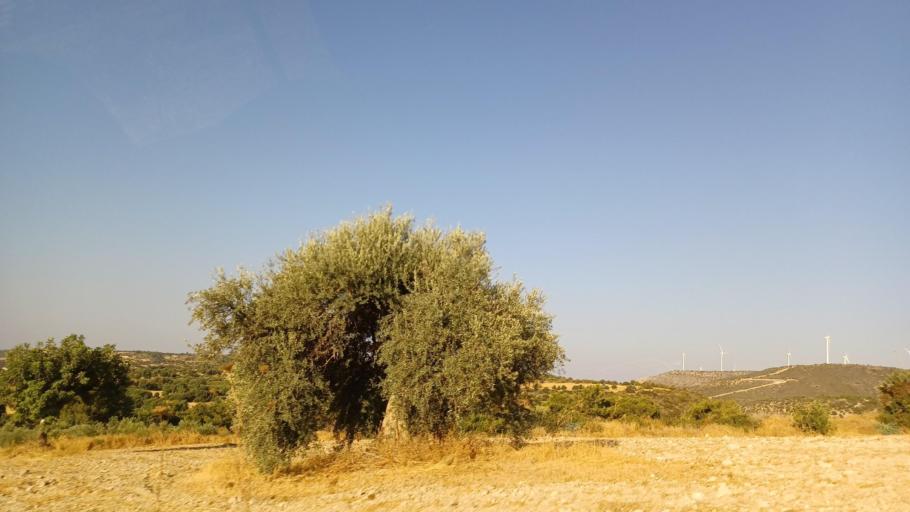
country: CY
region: Limassol
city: Pissouri
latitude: 34.7177
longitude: 32.6747
